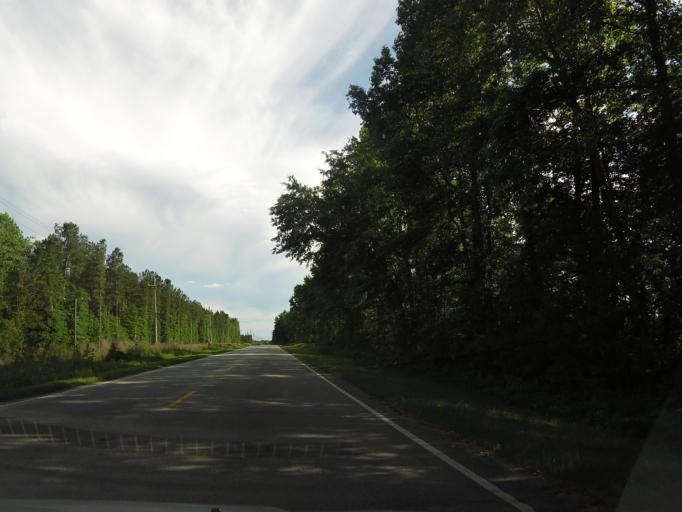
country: US
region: South Carolina
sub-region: Allendale County
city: Fairfax
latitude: 32.8905
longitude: -81.2381
